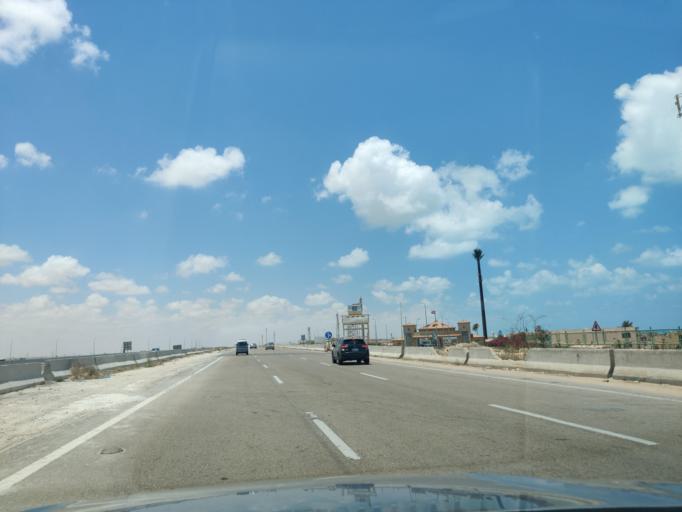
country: EG
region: Muhafazat Matruh
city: Al `Alamayn
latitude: 30.8128
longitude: 29.0584
